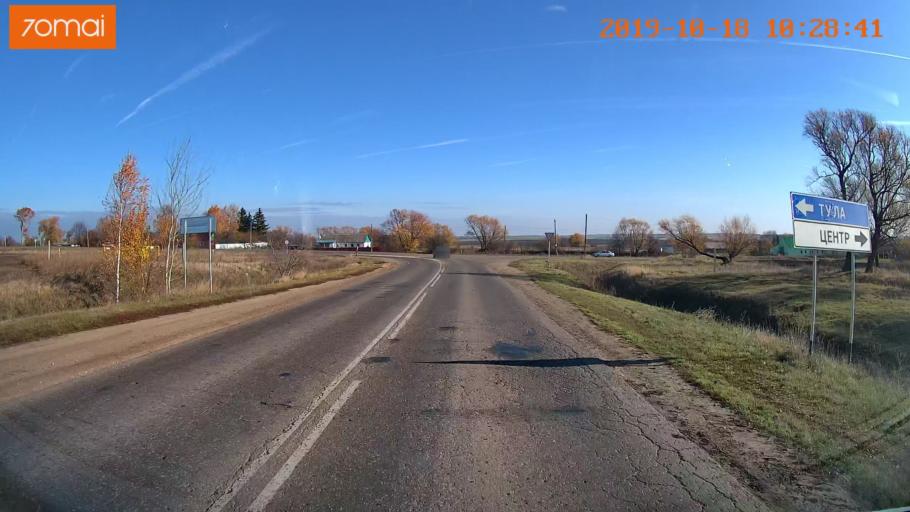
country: RU
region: Tula
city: Kurkino
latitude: 53.4464
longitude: 38.6589
